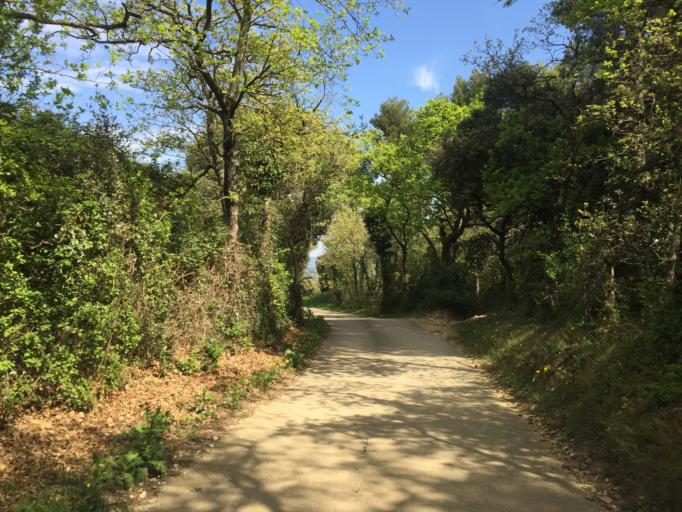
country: FR
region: Provence-Alpes-Cote d'Azur
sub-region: Departement du Vaucluse
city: Courthezon
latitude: 44.0657
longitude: 4.8647
